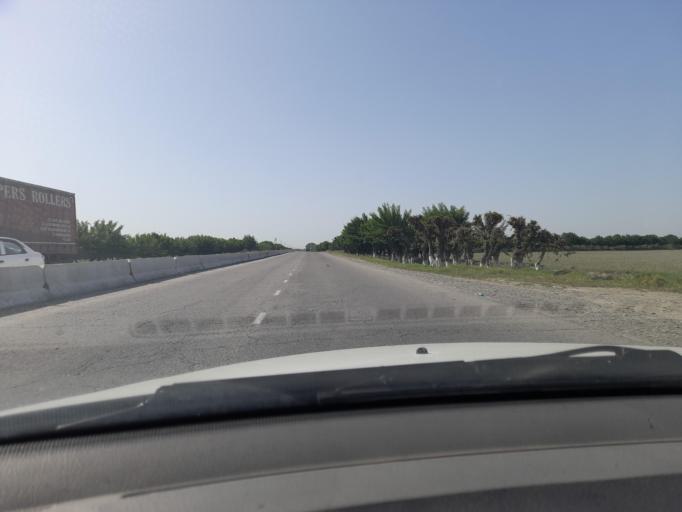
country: UZ
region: Samarqand
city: Daxbet
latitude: 39.8248
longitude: 66.8407
